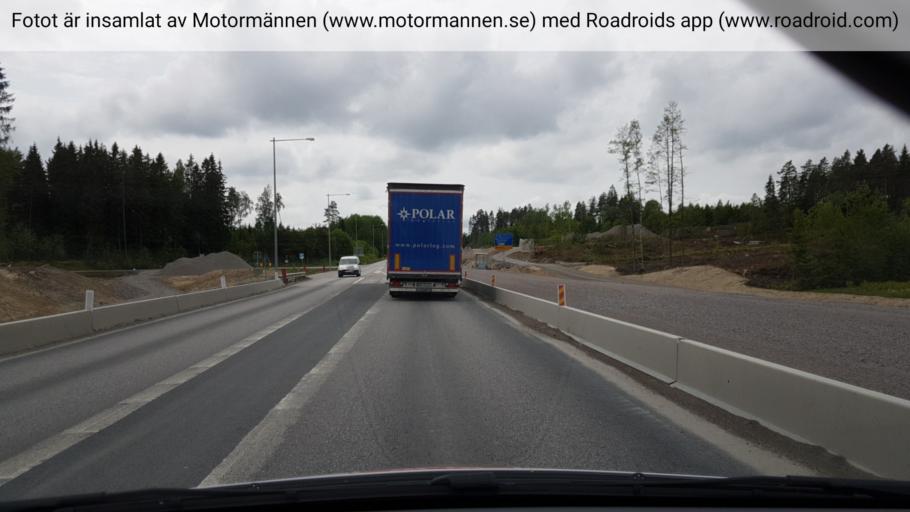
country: SE
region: OErebro
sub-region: Askersunds Kommun
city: Askersund
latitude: 58.9167
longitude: 14.9792
